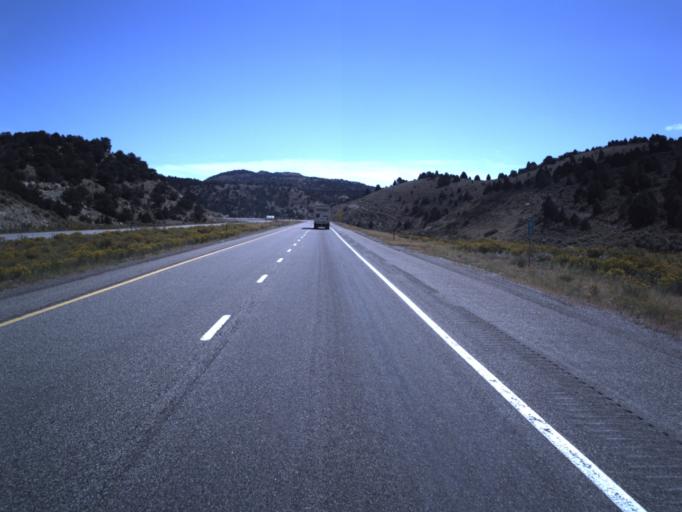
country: US
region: Utah
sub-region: Sevier County
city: Salina
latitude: 38.8045
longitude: -111.5271
